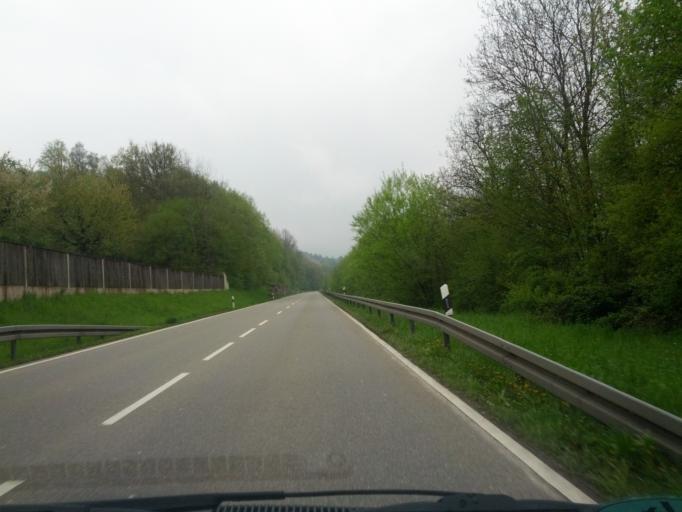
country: DE
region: Baden-Wuerttemberg
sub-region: Freiburg Region
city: Wehr
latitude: 47.6276
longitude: 7.8971
